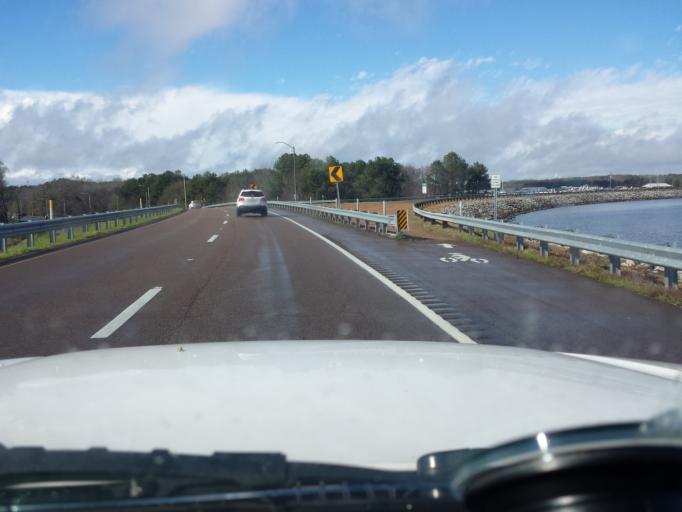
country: US
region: Mississippi
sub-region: Madison County
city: Ridgeland
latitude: 32.4110
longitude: -90.0857
